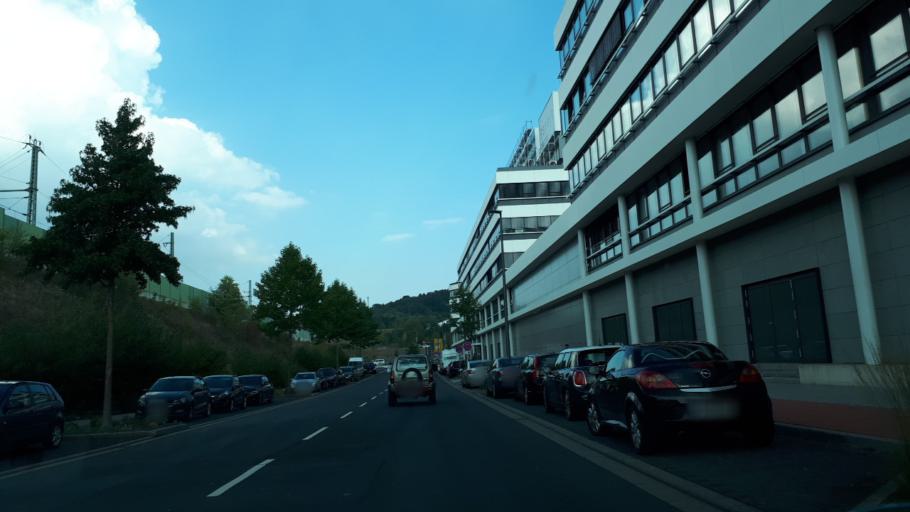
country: DE
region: Rheinland-Pfalz
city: Montabaur
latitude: 50.4441
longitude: 7.8277
